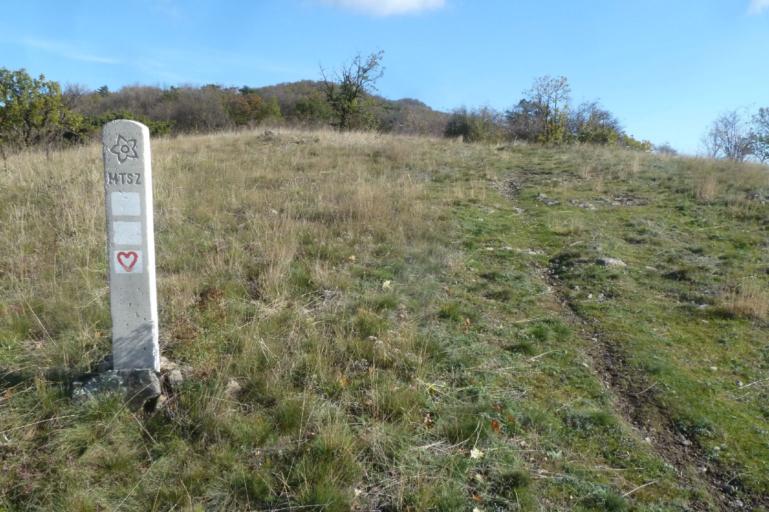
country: HU
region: Nograd
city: Szurdokpuspoki
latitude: 47.8672
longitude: 19.7288
